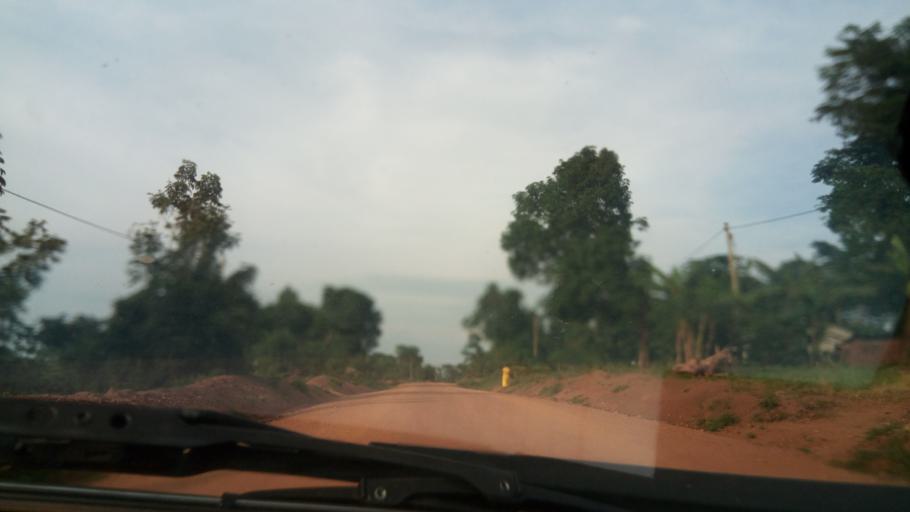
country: UG
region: Central Region
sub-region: Mityana District
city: Mityana
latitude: 0.5284
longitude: 32.1672
